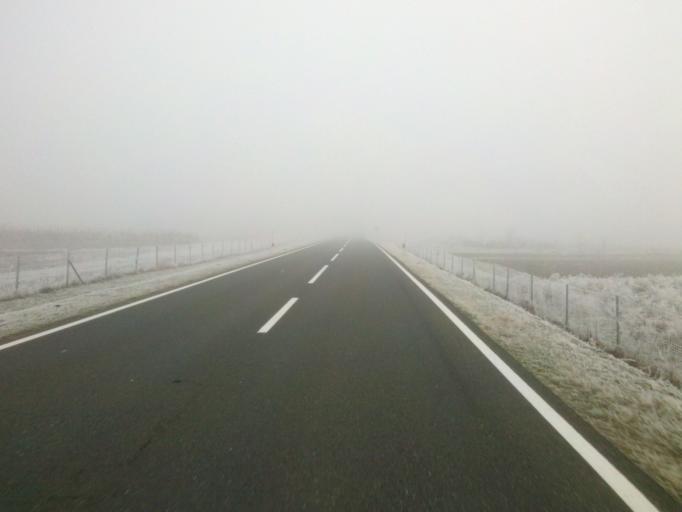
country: HR
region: Varazdinska
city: Jalkovec
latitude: 46.2657
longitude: 16.3254
